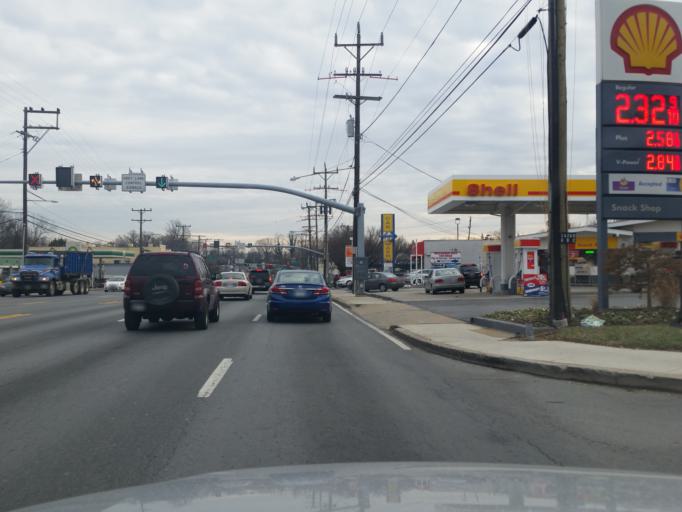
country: US
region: Maryland
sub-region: Montgomery County
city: Forest Glen
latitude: 39.0110
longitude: -77.0412
